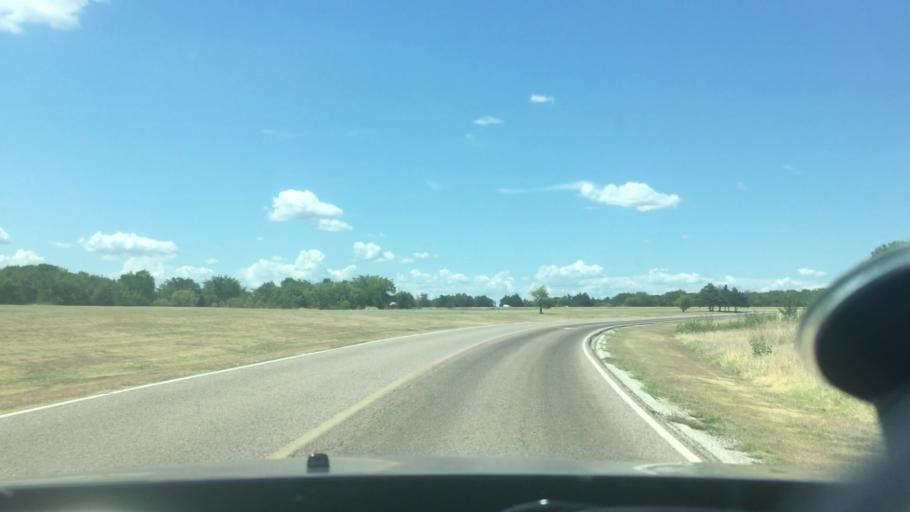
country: US
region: Oklahoma
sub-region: Marshall County
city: Kingston
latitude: 33.9929
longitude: -96.6414
